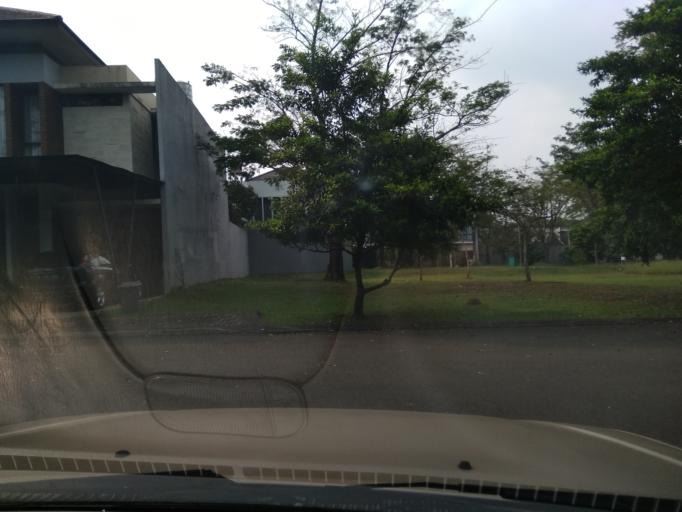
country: ID
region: West Java
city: Serpong
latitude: -6.3137
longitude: 106.6462
